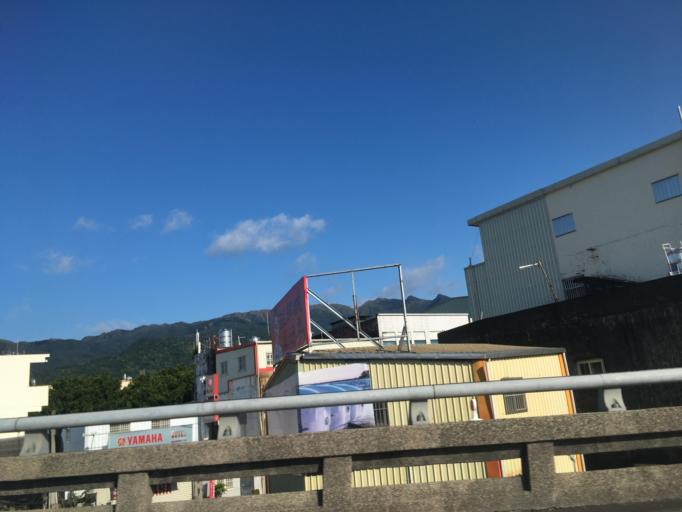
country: TW
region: Taiwan
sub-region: Yilan
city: Yilan
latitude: 24.8528
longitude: 121.8209
